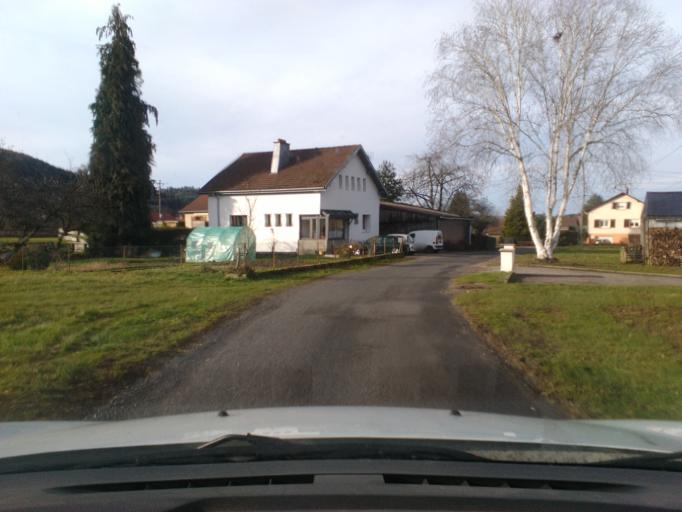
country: FR
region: Lorraine
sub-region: Departement des Vosges
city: Fraize
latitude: 48.1724
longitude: 6.9804
